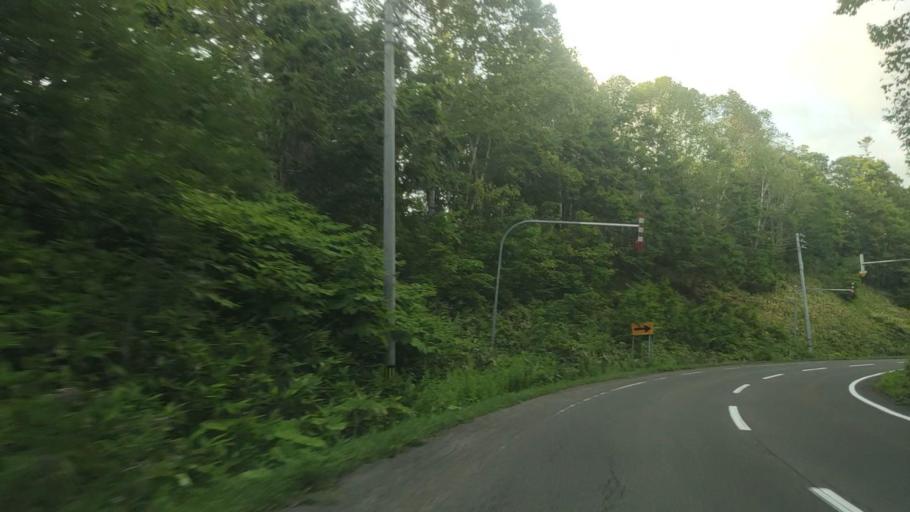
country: JP
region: Hokkaido
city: Bibai
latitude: 43.1749
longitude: 142.0683
